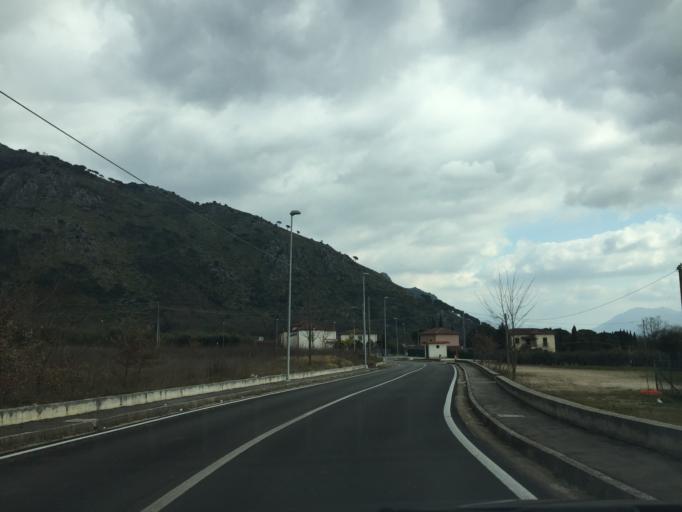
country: IT
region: Latium
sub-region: Provincia di Frosinone
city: Villa Santa Lucia
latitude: 41.4950
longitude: 13.7732
